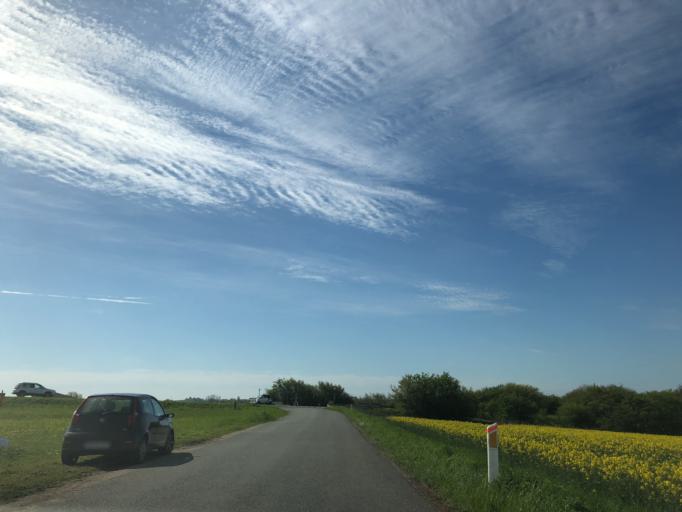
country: DK
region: Zealand
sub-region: Slagelse Kommune
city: Forlev
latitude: 55.3786
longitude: 11.2979
